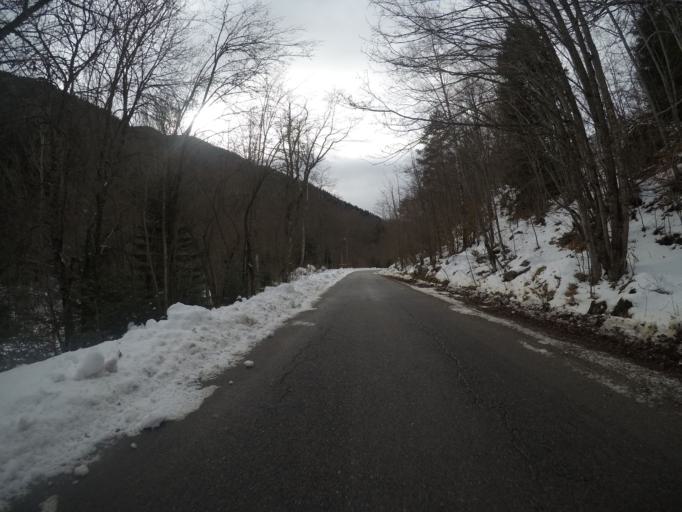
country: BG
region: Kyustendil
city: Sapareva Banya
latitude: 42.1424
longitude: 23.3569
